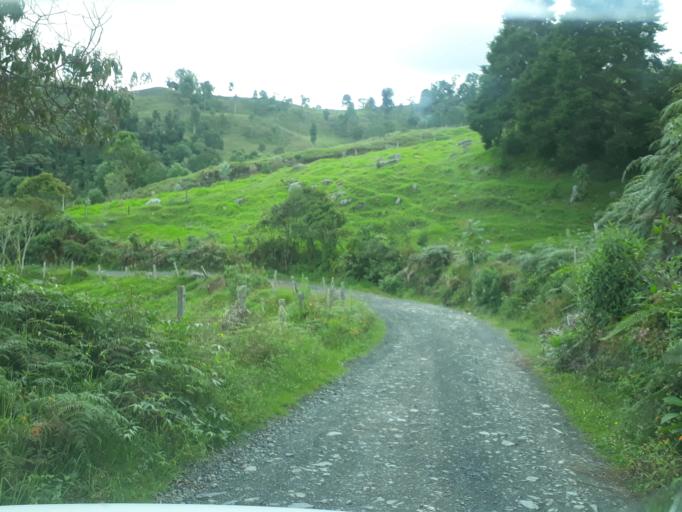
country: CO
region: Cundinamarca
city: Carmen de Carupa
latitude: 5.3490
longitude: -74.0606
